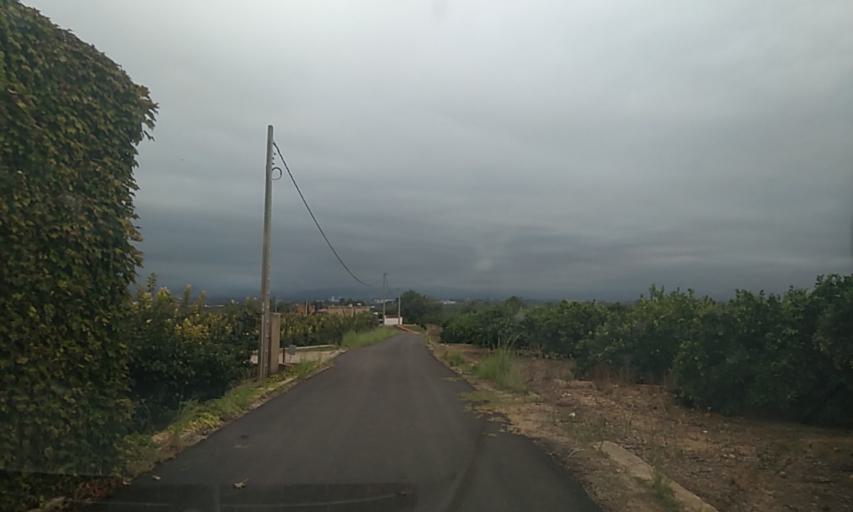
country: ES
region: Valencia
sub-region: Provincia de Valencia
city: Benimodo
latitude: 39.1942
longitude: -0.5636
